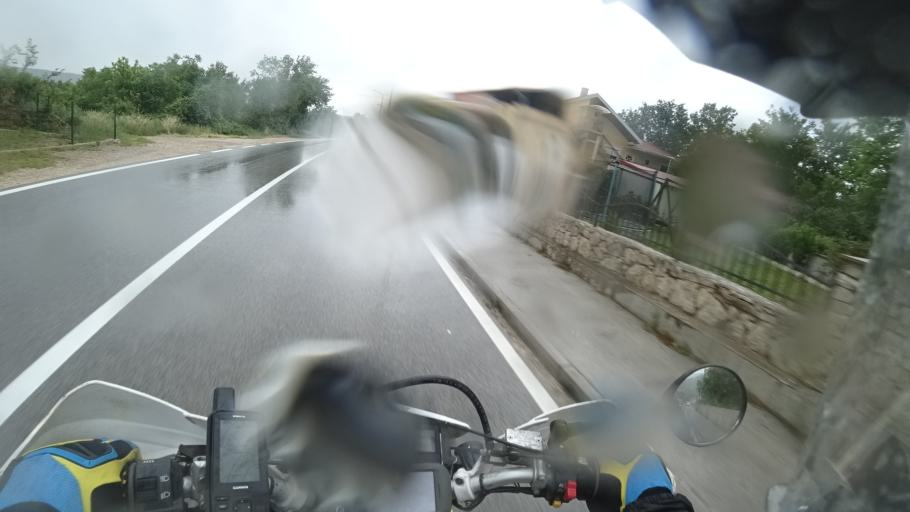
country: HR
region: Sibensko-Kniniska
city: Knin
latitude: 44.0436
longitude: 16.2196
